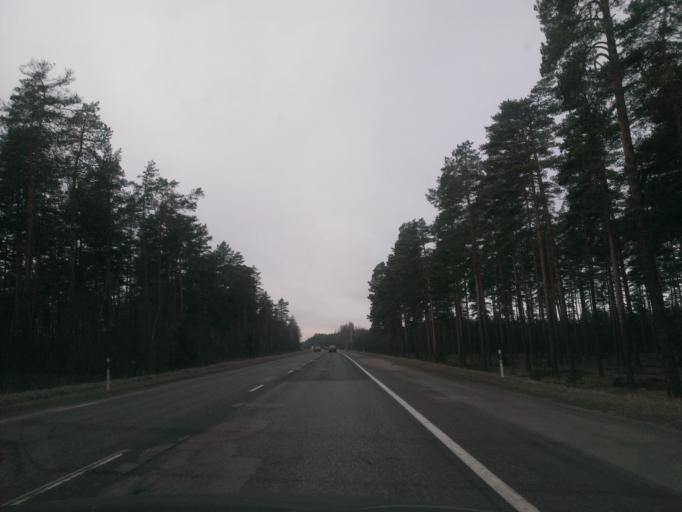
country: LV
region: Incukalns
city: Vangazi
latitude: 57.0722
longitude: 24.4954
